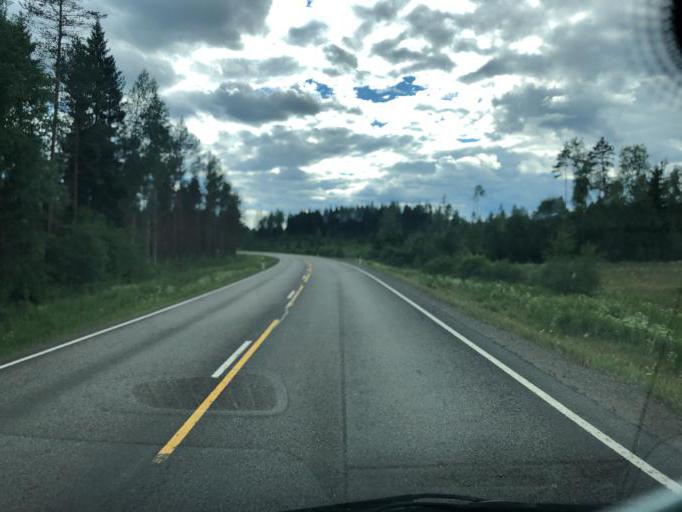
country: FI
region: Kymenlaakso
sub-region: Kouvola
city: Kouvola
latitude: 61.0202
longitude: 26.9619
